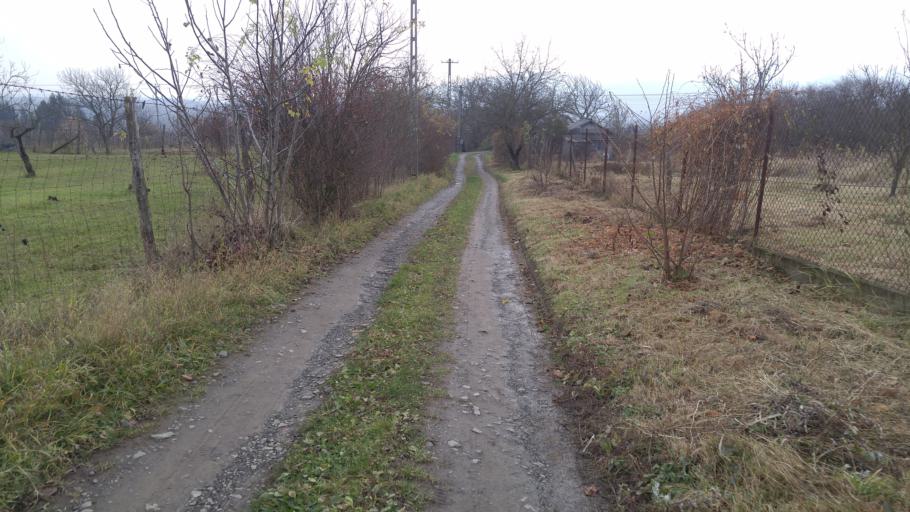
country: HU
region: Pest
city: Kismaros
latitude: 47.8277
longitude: 18.9918
